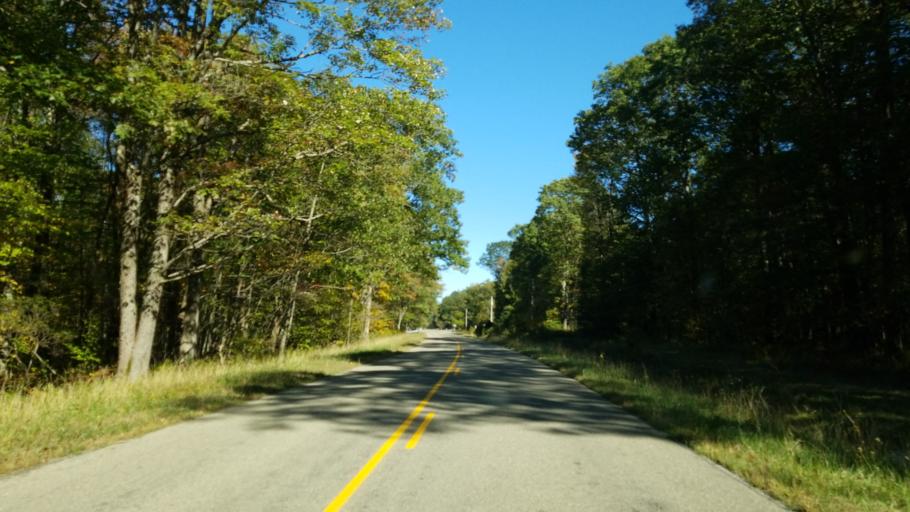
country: US
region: Pennsylvania
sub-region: Clearfield County
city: Shiloh
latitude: 41.2506
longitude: -78.3422
